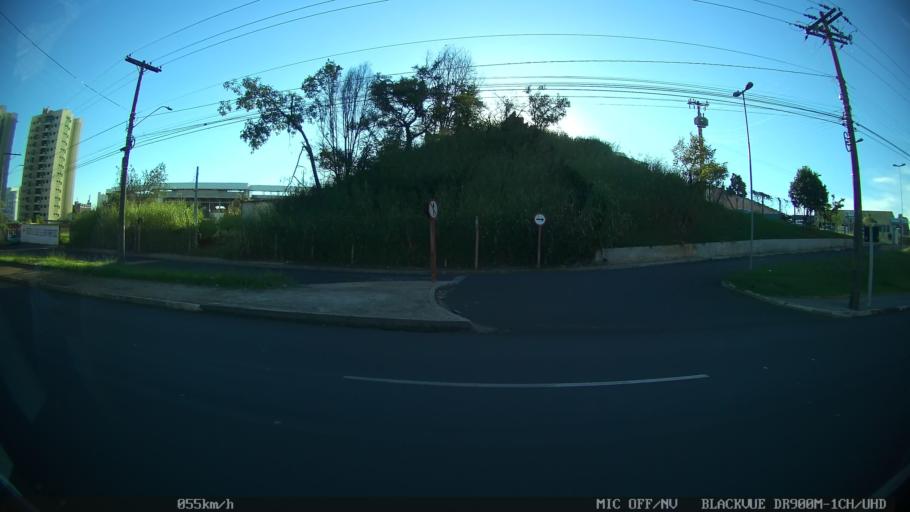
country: BR
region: Sao Paulo
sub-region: Araraquara
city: Araraquara
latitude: -21.7752
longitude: -48.1676
